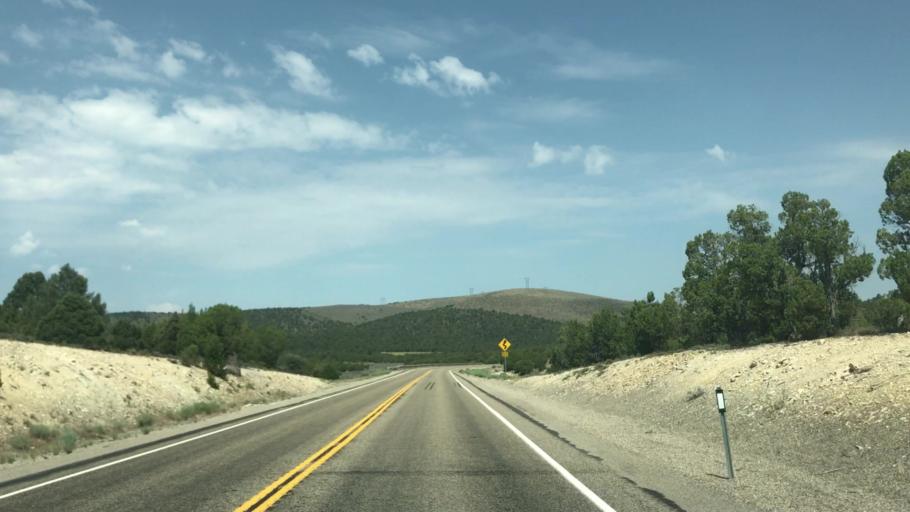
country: US
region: Nevada
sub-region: White Pine County
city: Ely
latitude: 39.3901
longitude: -115.0790
